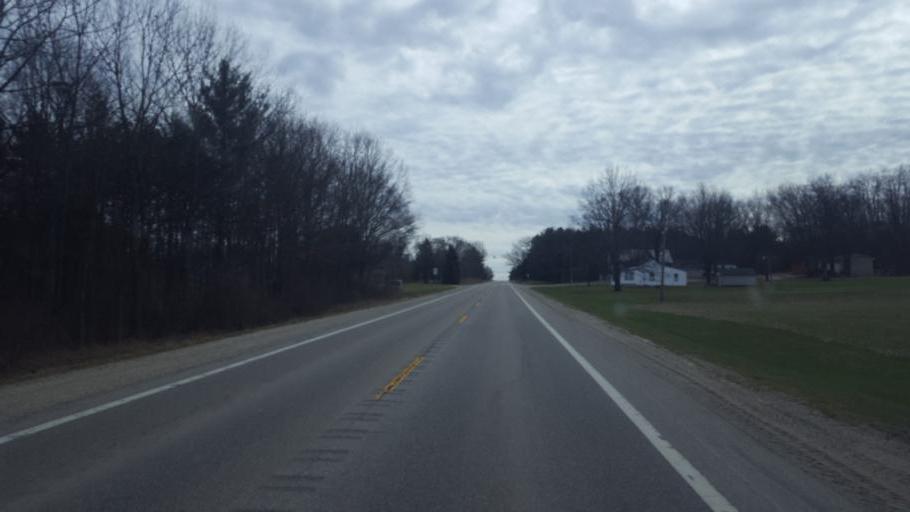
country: US
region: Michigan
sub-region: Isabella County
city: Lake Isabella
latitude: 43.6843
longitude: -85.1465
